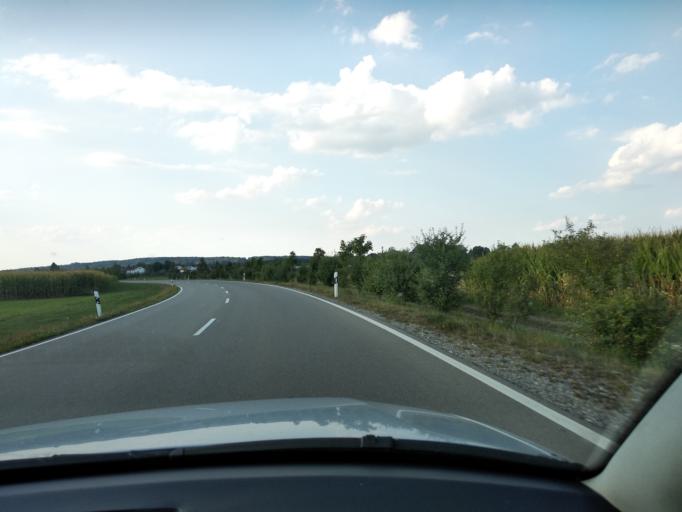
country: DE
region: Bavaria
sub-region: Swabia
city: Trunkelsberg
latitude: 47.9951
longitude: 10.2175
